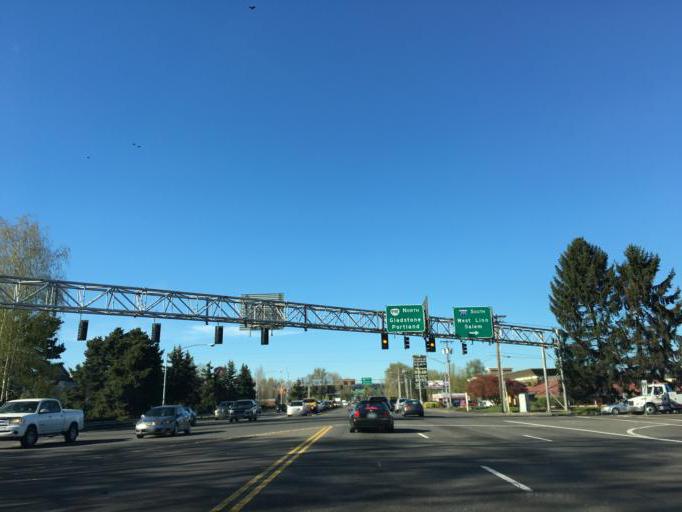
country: US
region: Oregon
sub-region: Clackamas County
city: Oregon City
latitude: 45.3662
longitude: -122.6008
